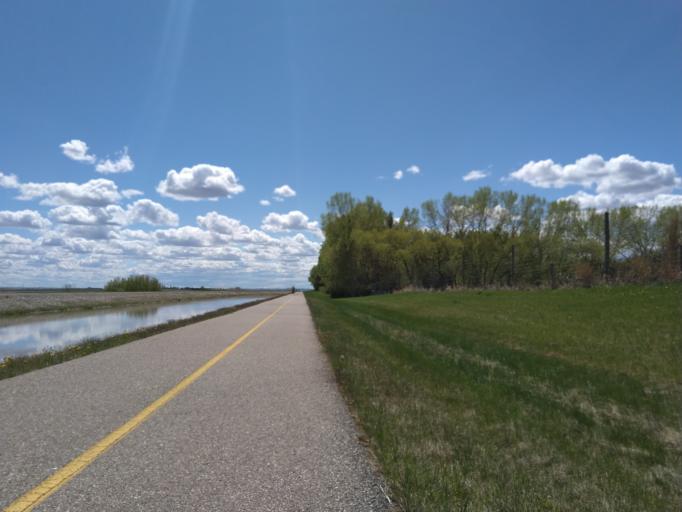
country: CA
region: Alberta
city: Chestermere
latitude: 50.9948
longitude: -113.8615
